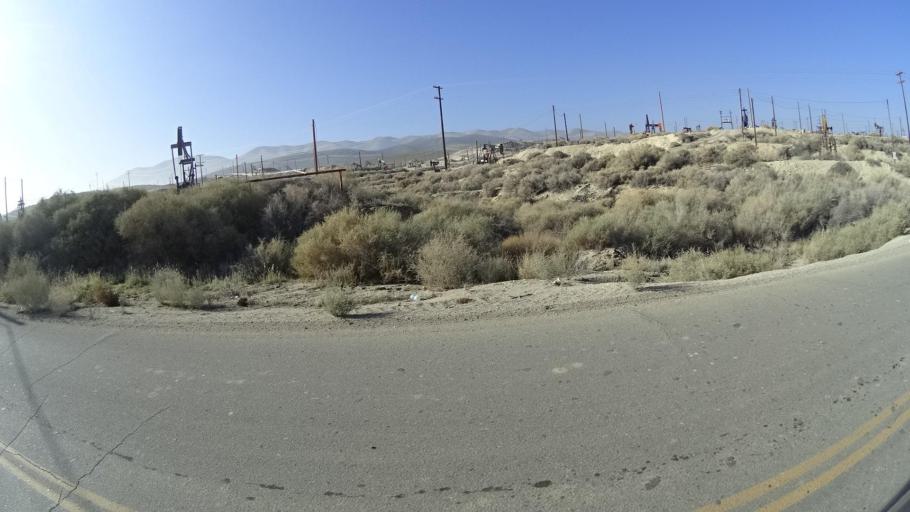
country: US
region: California
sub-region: Kern County
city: Taft Heights
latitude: 35.2059
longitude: -119.5979
